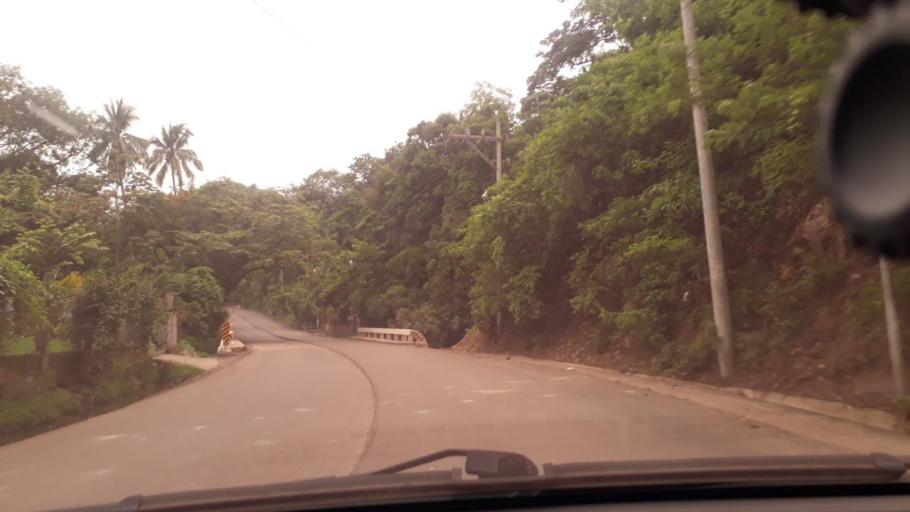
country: GT
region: Chiquimula
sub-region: Municipio de San Juan Ermita
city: San Juan Ermita
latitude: 14.7631
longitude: -89.4355
